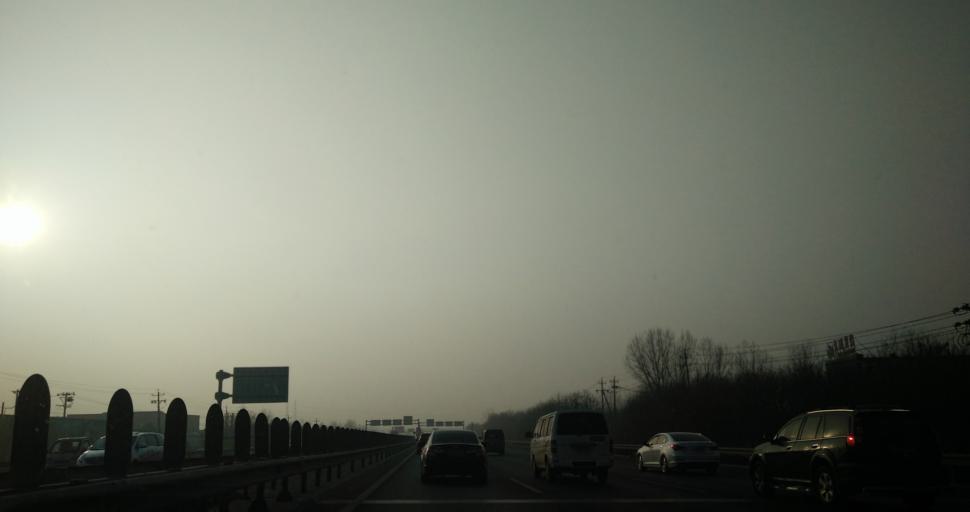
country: CN
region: Beijing
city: Nanyuan
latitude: 39.7587
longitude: 116.3860
